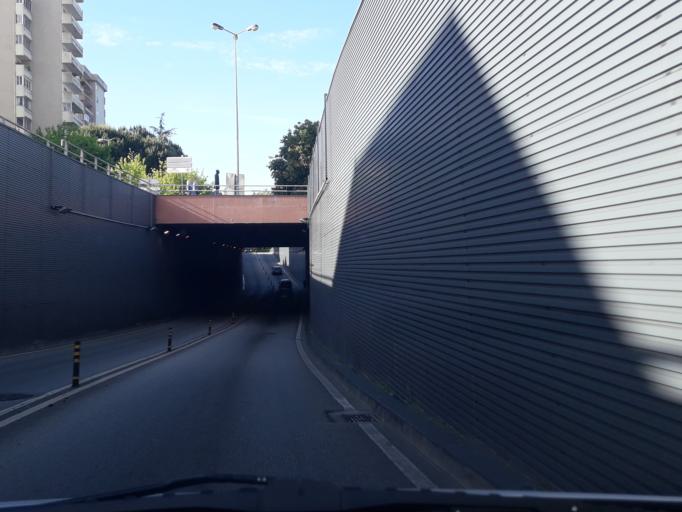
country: PT
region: Braga
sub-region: Vila Nova de Famalicao
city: Vila Nova de Famalicao
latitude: 41.4089
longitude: -8.5167
